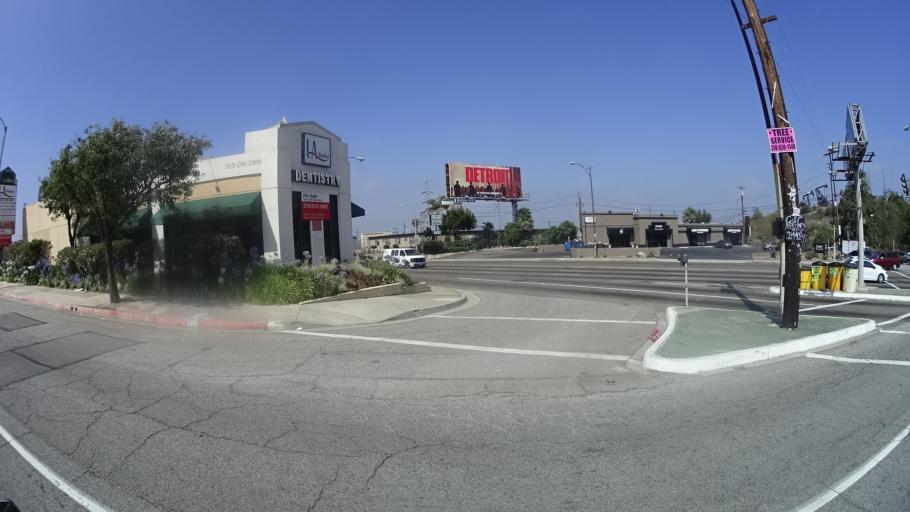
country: US
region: California
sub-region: Los Angeles County
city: View Park-Windsor Hills
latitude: 33.9968
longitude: -118.3577
